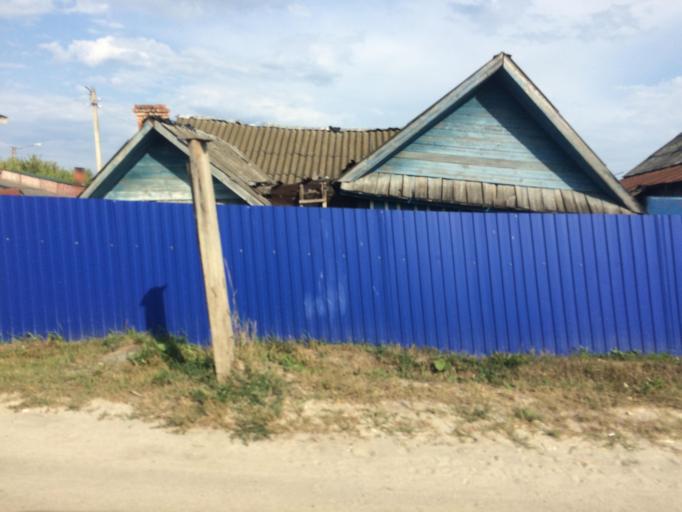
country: RU
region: Mariy-El
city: Yoshkar-Ola
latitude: 56.5492
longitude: 47.9834
